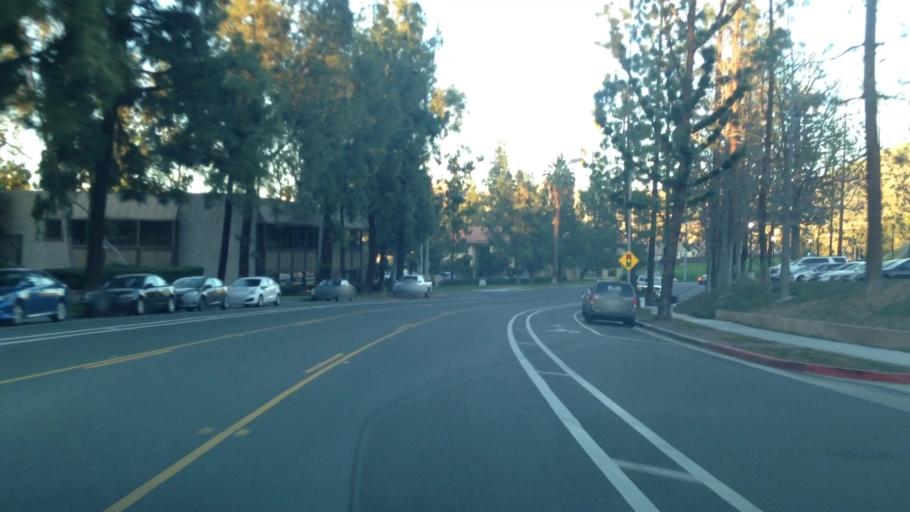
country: US
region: California
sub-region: Riverside County
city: Highgrove
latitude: 33.9573
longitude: -117.3325
